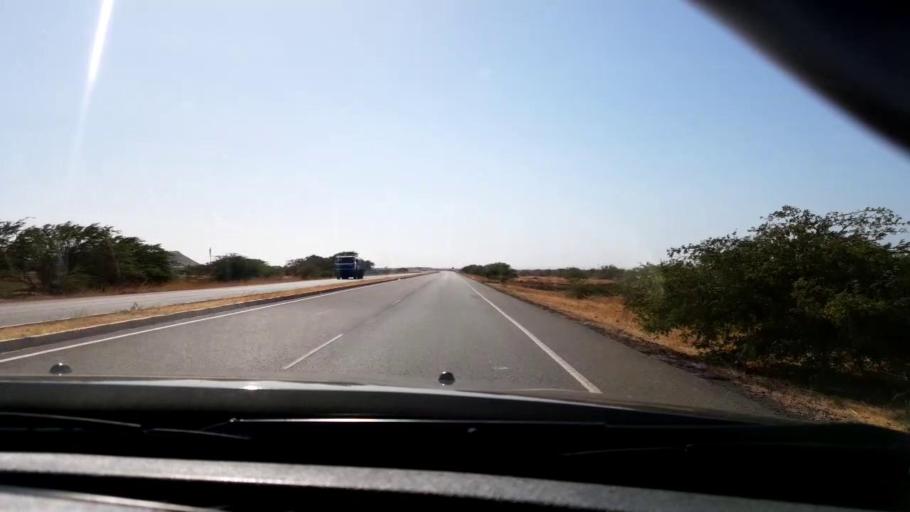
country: CV
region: Praia
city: Praia
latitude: 14.9467
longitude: -23.4903
